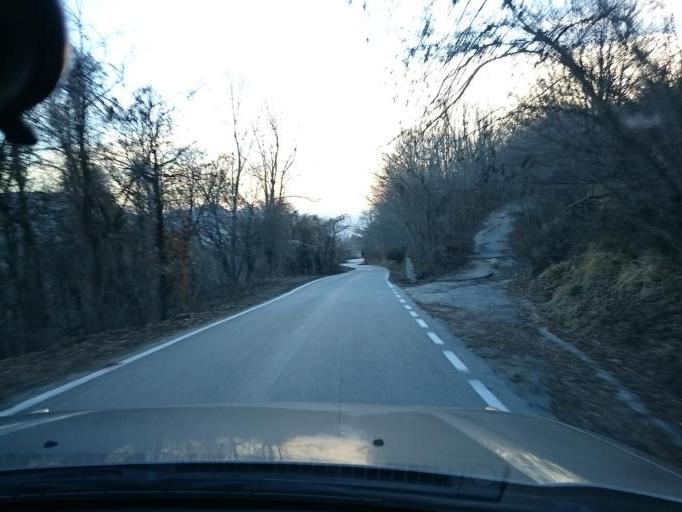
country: IT
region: Veneto
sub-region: Provincia di Padova
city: Bastia
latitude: 45.3581
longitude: 11.6575
